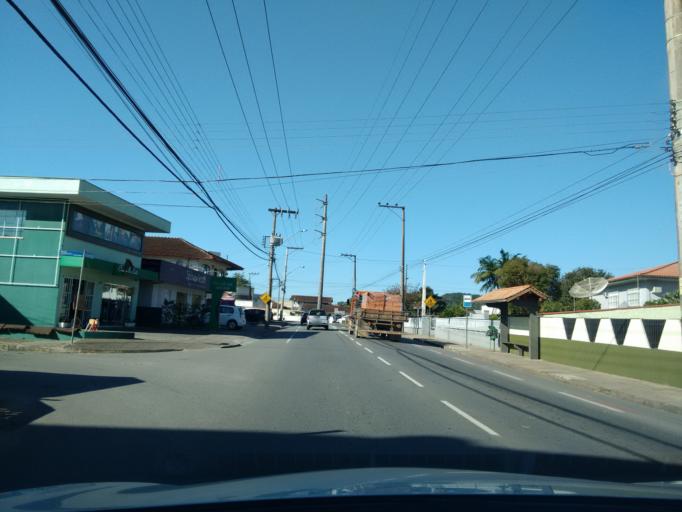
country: BR
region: Santa Catarina
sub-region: Jaragua Do Sul
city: Jaragua do Sul
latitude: -26.4910
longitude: -49.0606
